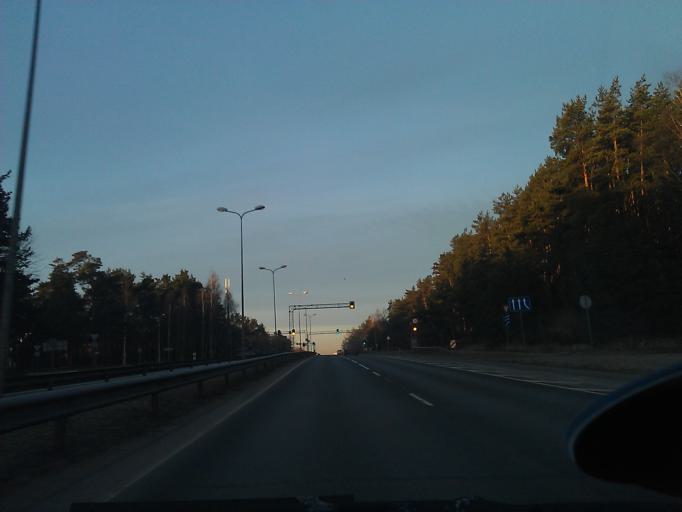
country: LV
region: Riga
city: Bergi
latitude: 57.0003
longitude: 24.2771
